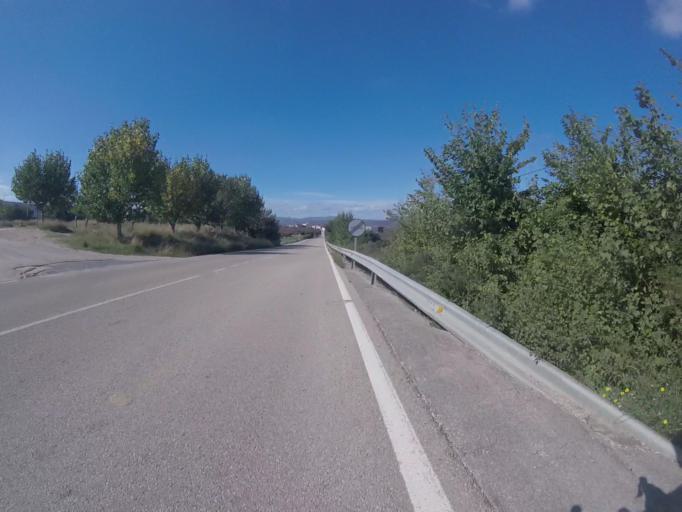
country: ES
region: Valencia
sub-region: Provincia de Castello
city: Albocasser
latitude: 40.3575
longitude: 0.0373
